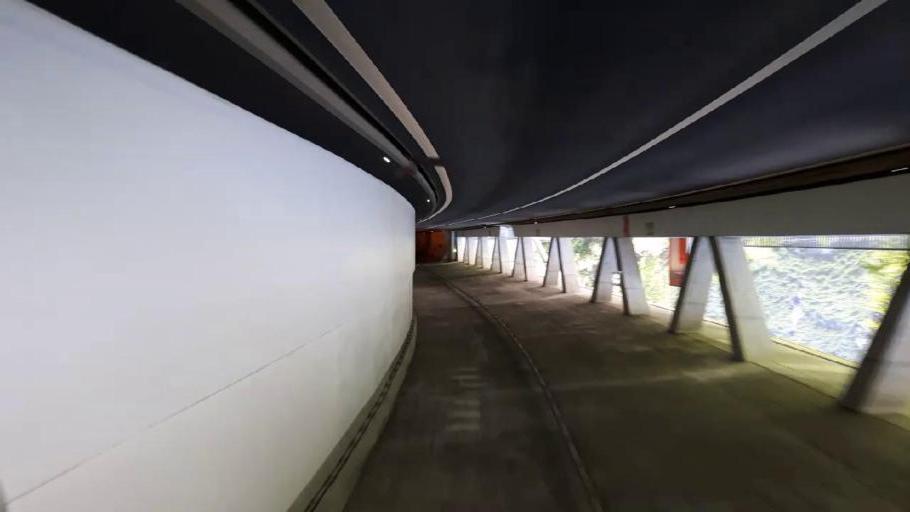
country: CH
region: Valais
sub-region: Brig District
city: Brig
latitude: 46.2516
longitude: 8.0412
